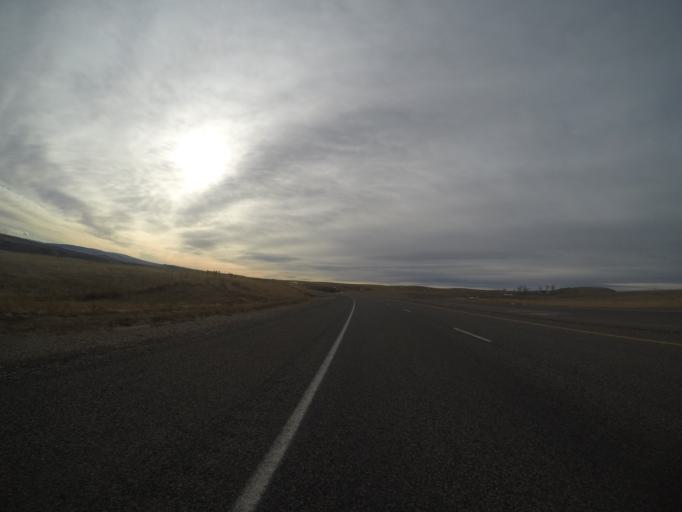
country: US
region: Montana
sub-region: Yellowstone County
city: Laurel
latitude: 45.5533
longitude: -108.8624
